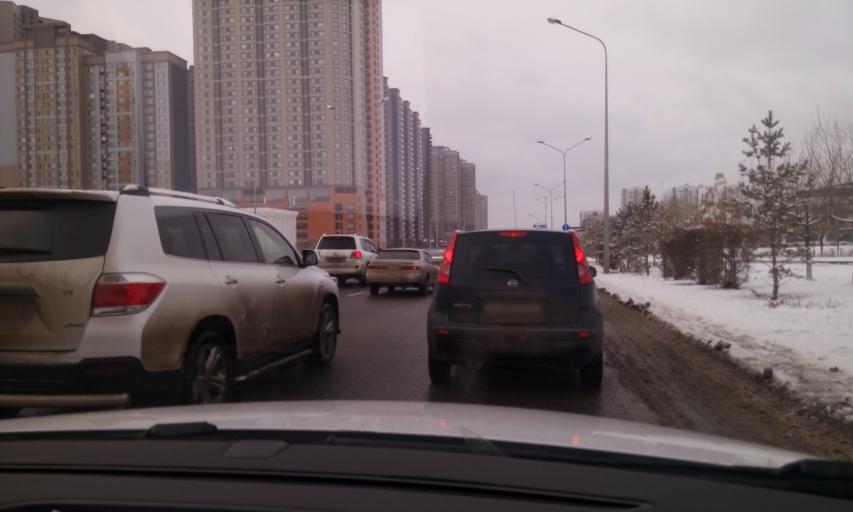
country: KZ
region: Astana Qalasy
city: Astana
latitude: 51.1273
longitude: 71.4731
